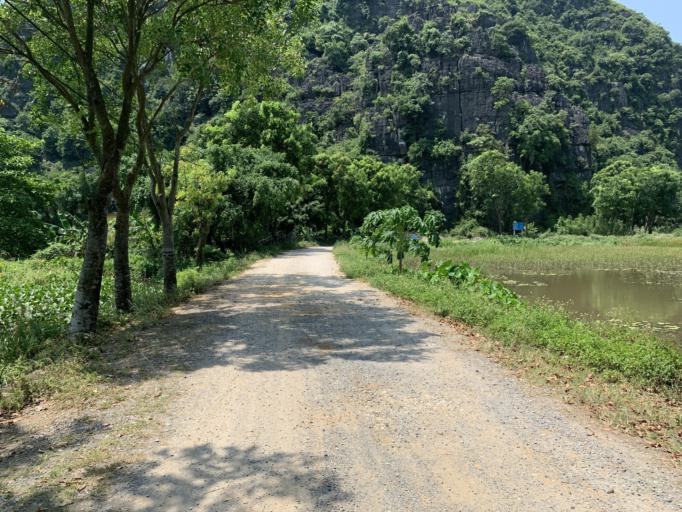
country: VN
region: Ninh Binh
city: Thanh Pho Ninh Binh
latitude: 20.2221
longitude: 105.9314
